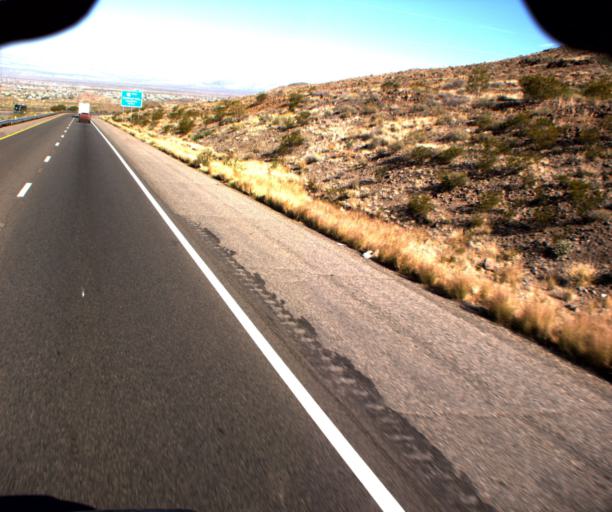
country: US
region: Arizona
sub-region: Mohave County
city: Kingman
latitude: 35.2111
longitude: -114.1085
